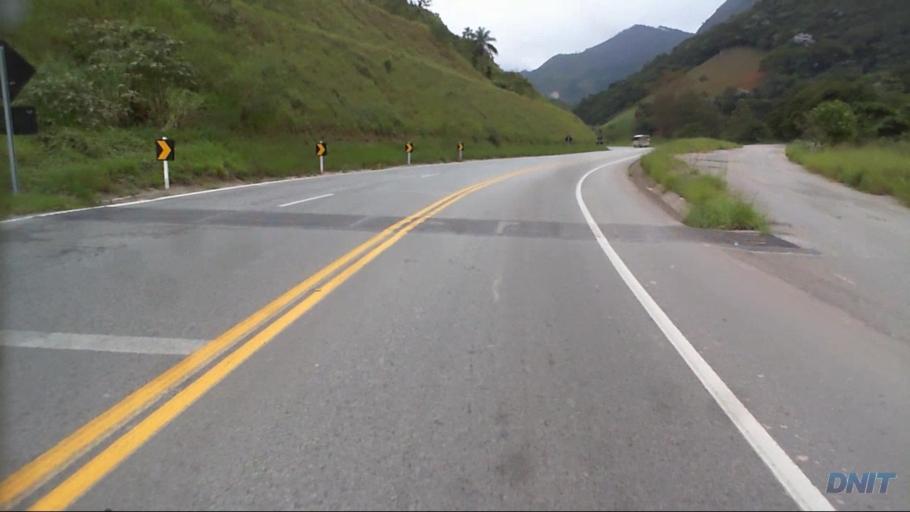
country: BR
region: Minas Gerais
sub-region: Nova Era
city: Nova Era
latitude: -19.6425
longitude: -42.9187
